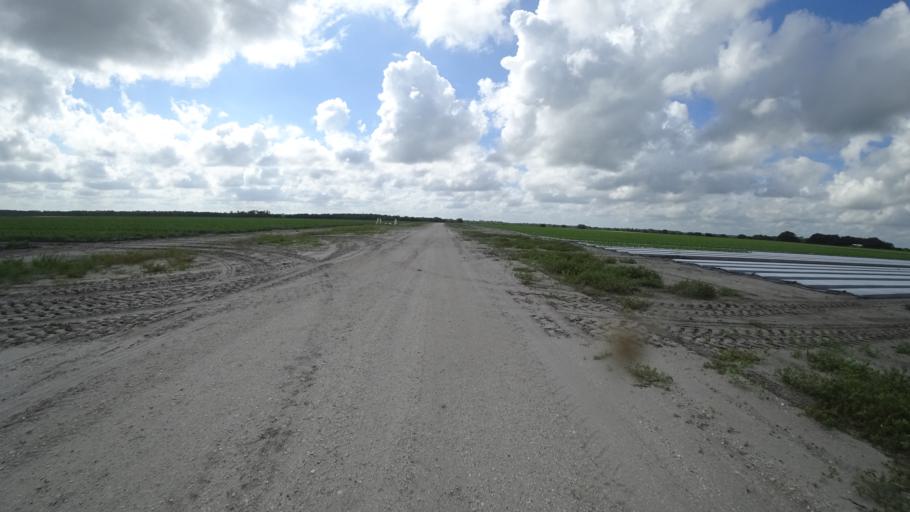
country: US
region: Florida
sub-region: Sarasota County
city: Lake Sarasota
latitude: 27.4063
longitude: -82.2117
